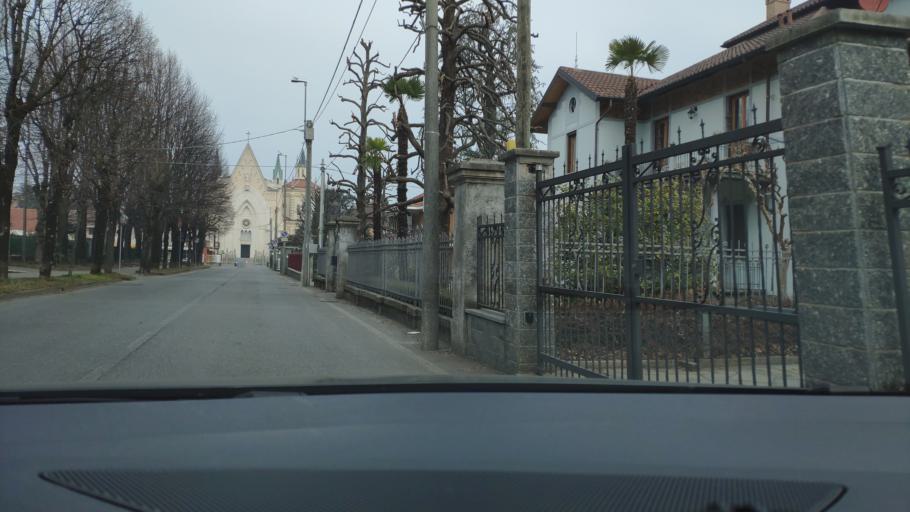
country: IT
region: Piedmont
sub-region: Provincia di Torino
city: Pianezza
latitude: 45.1122
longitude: 7.5433
